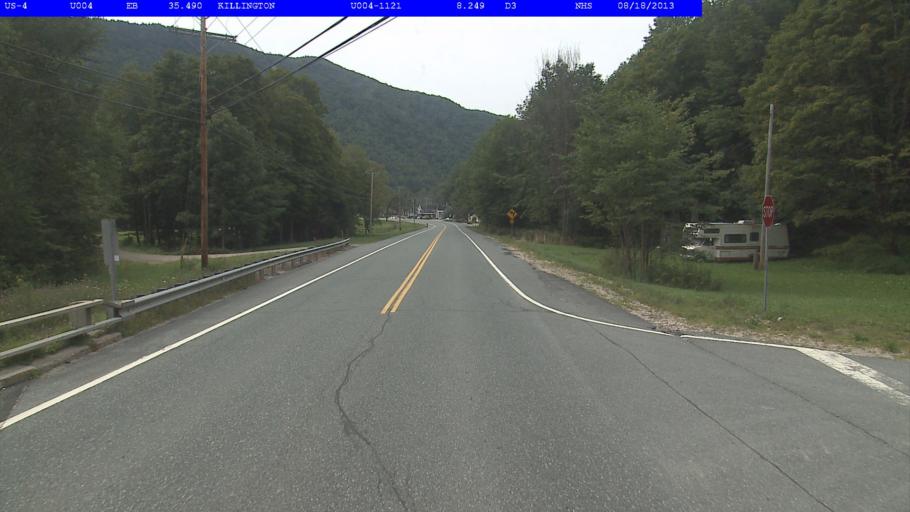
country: US
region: Vermont
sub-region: Rutland County
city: Rutland
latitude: 43.6038
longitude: -72.7509
